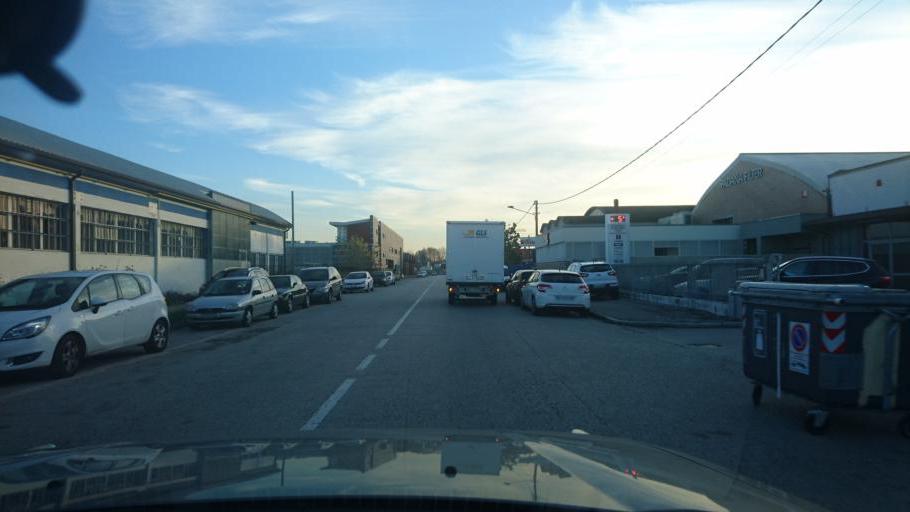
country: IT
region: Veneto
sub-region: Provincia di Padova
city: Noventa
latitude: 45.4140
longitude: 11.9364
